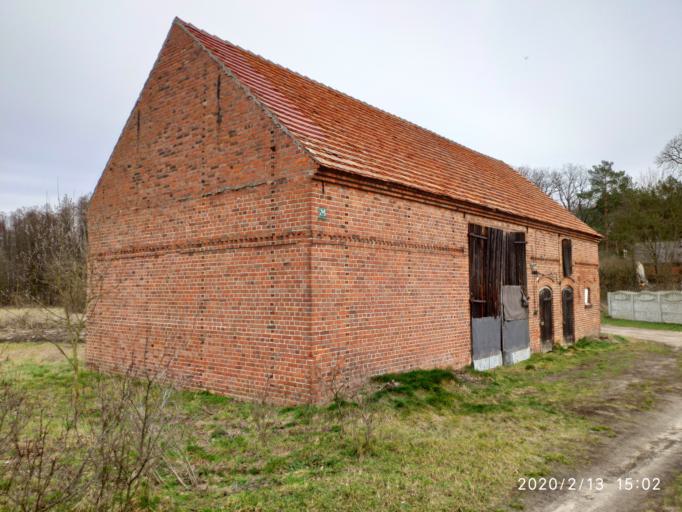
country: PL
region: Lubusz
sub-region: Powiat zielonogorski
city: Zabor
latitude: 51.9748
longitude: 15.6452
